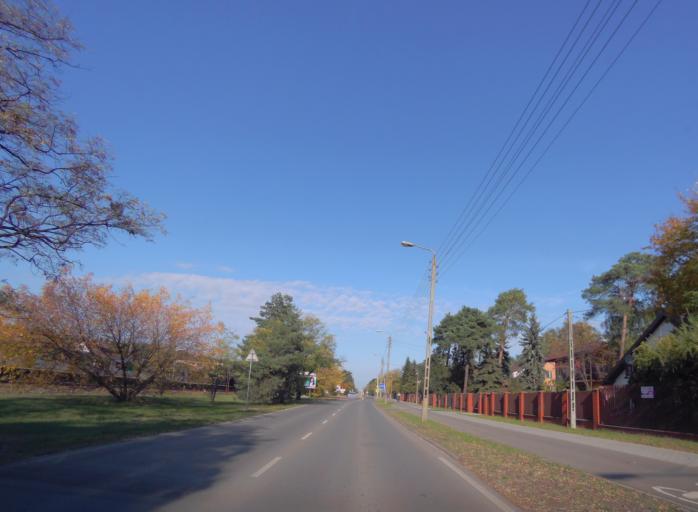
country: PL
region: Masovian Voivodeship
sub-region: Powiat otwocki
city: Jozefow
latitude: 52.1477
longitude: 21.2256
